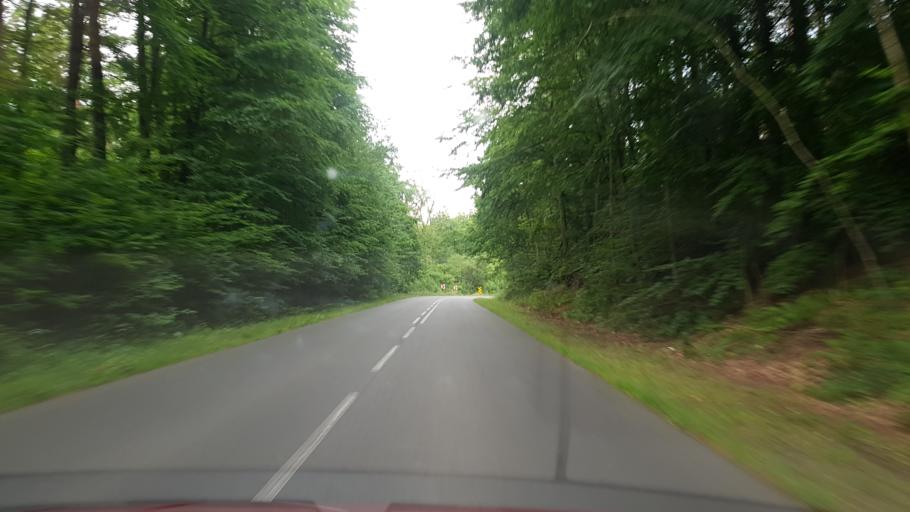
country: PL
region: West Pomeranian Voivodeship
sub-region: Powiat gryficki
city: Gryfice
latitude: 53.8518
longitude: 15.1096
